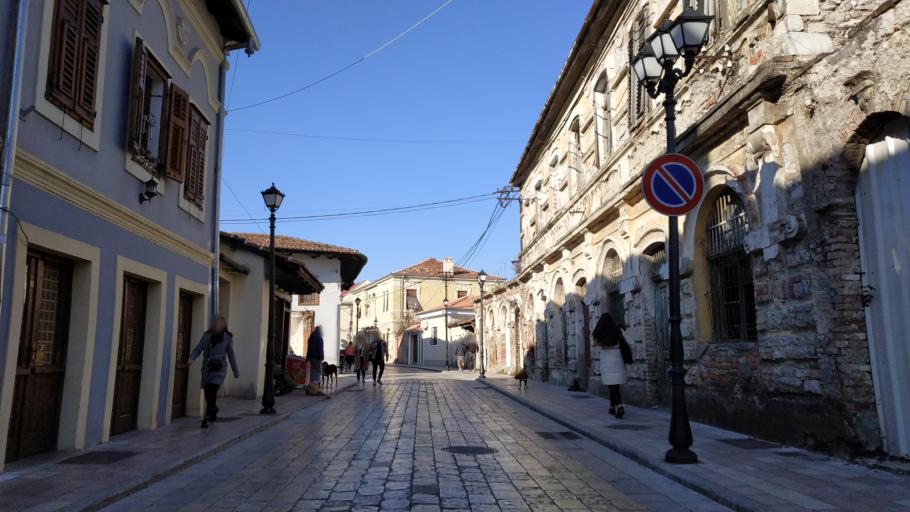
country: AL
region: Shkoder
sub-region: Rrethi i Shkodres
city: Shkoder
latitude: 42.0671
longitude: 19.5177
